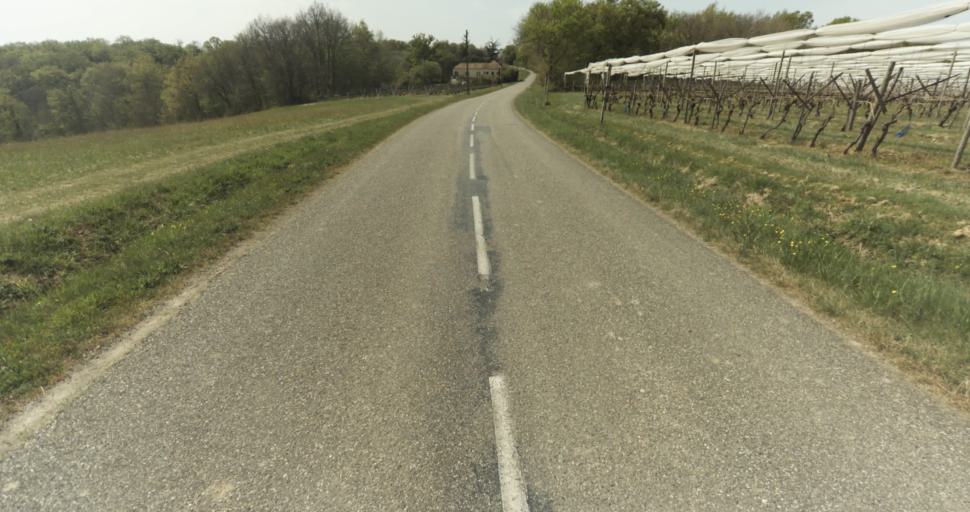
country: FR
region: Midi-Pyrenees
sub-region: Departement du Tarn-et-Garonne
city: Moissac
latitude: 44.1675
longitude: 1.0839
